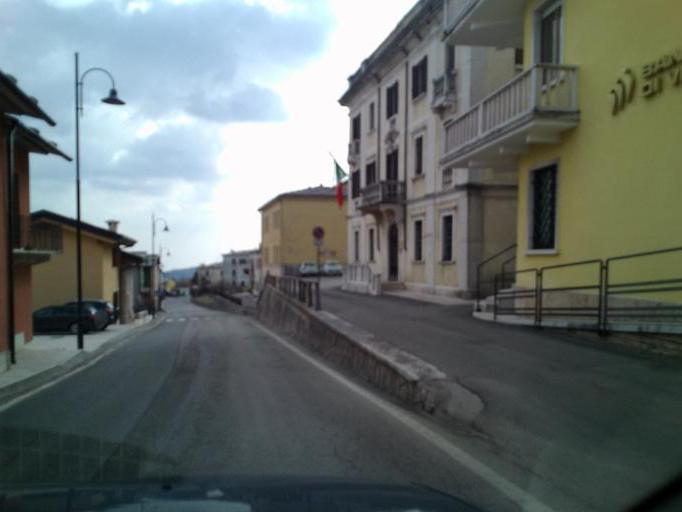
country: IT
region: Veneto
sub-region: Provincia di Verona
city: Sant'Anna d'Alfaedo
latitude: 45.6271
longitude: 10.9511
